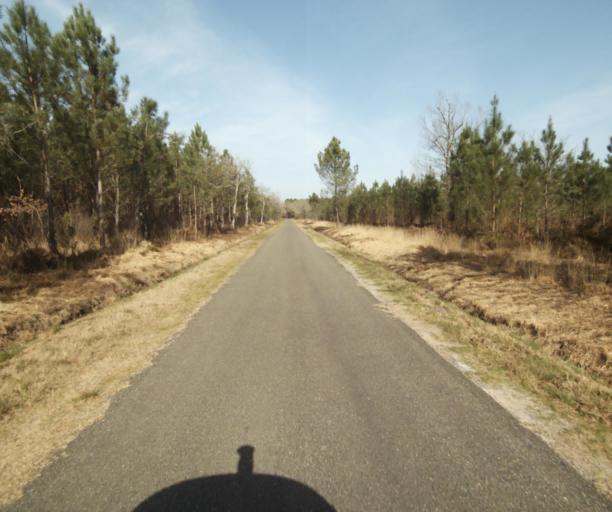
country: FR
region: Aquitaine
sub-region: Departement de la Gironde
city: Bazas
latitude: 44.2302
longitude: -0.2029
